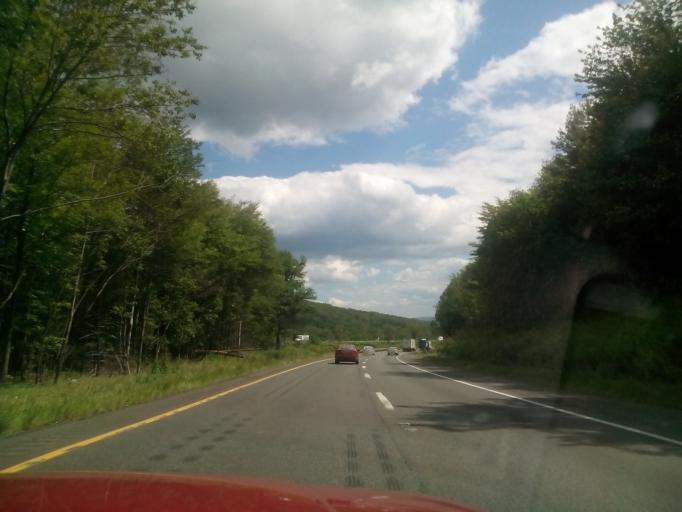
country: US
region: Pennsylvania
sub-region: Monroe County
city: Tannersville
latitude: 41.0550
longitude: -75.3198
